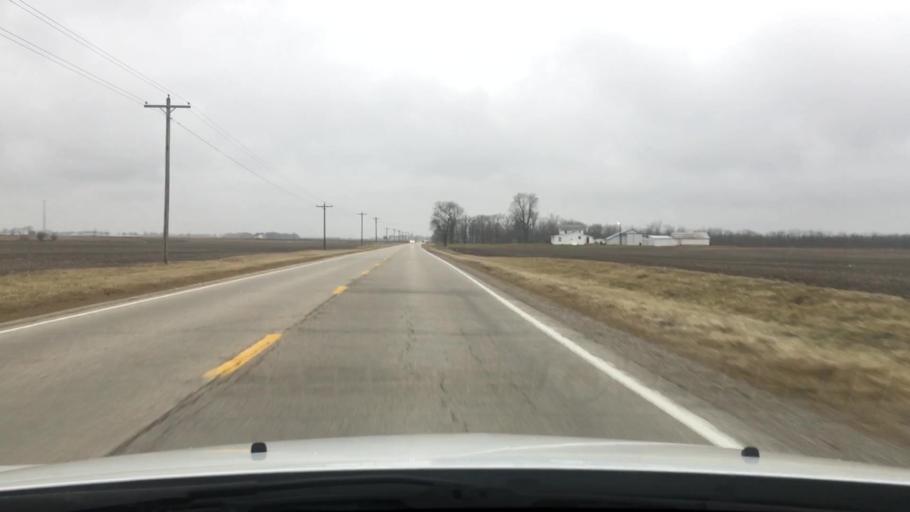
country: US
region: Illinois
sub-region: Iroquois County
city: Watseka
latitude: 40.8903
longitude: -87.7158
